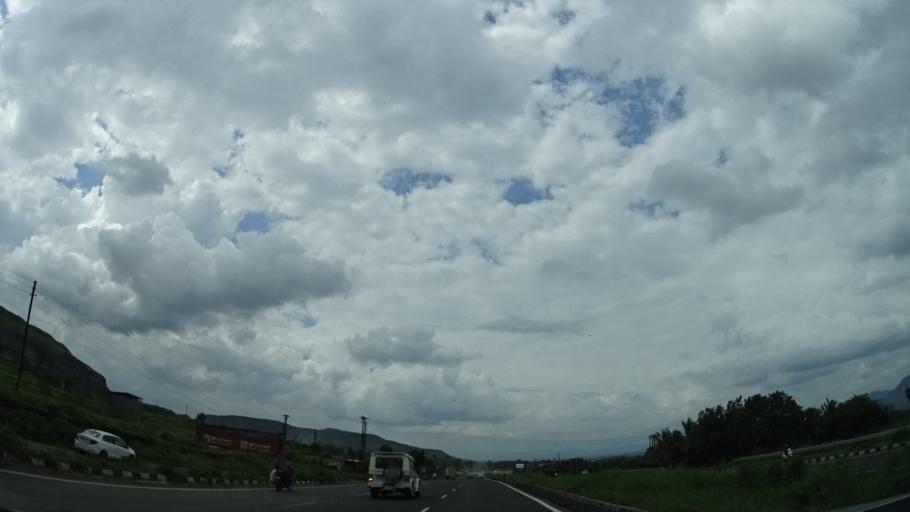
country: IN
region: Maharashtra
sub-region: Satara Division
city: Satara
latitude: 17.7579
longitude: 73.9927
